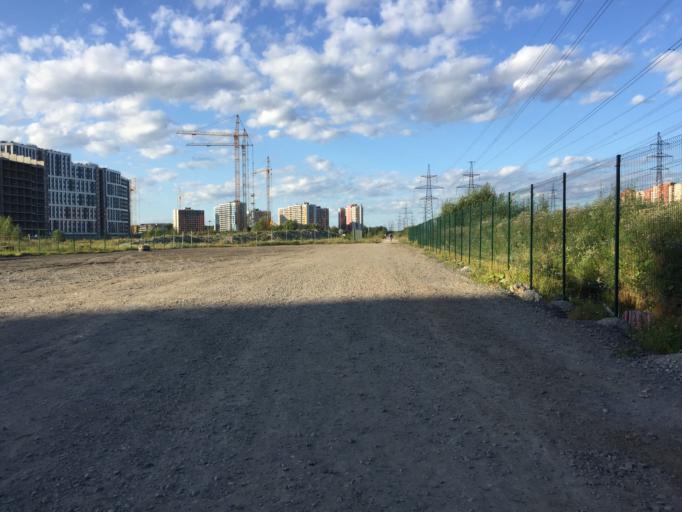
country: RU
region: Leningrad
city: Murino
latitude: 60.0611
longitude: 30.4456
